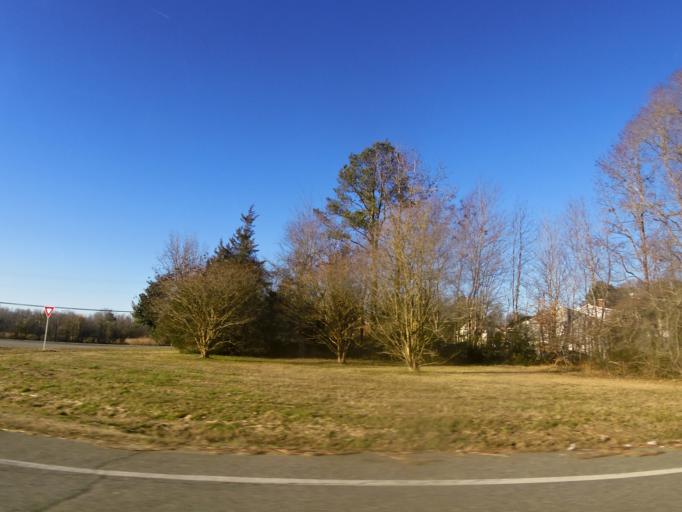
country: US
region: Virginia
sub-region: Isle of Wight County
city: Windsor
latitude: 36.6755
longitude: -76.7827
